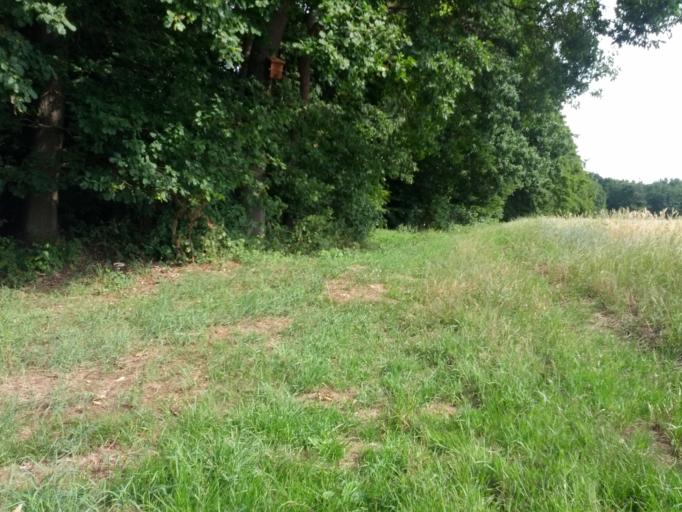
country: DE
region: Thuringia
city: Krauthausen
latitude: 50.9998
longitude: 10.2802
